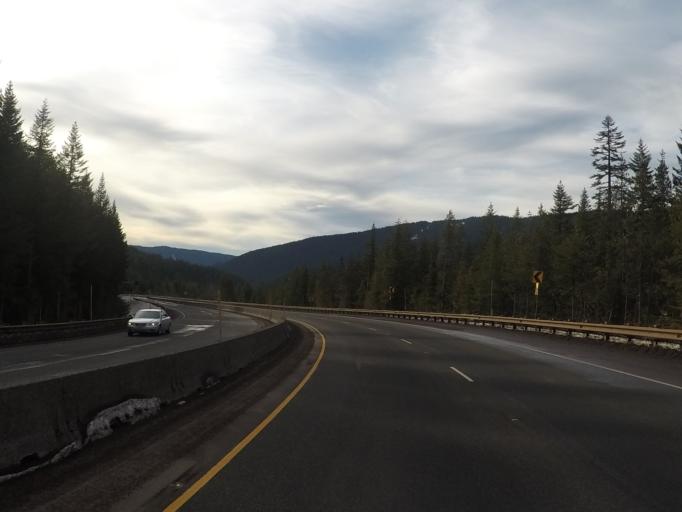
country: US
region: Oregon
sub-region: Clackamas County
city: Mount Hood Village
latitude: 45.3121
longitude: -121.7924
